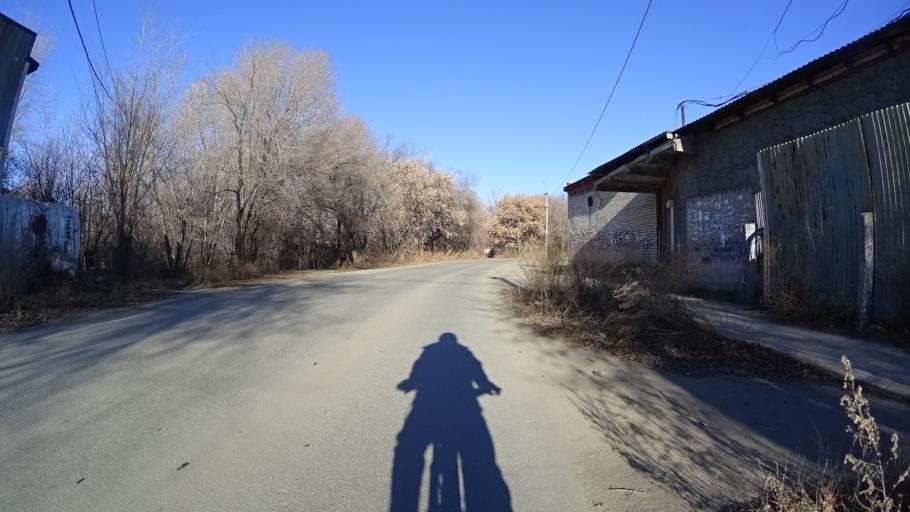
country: RU
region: Chelyabinsk
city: Troitsk
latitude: 54.0423
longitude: 61.6384
